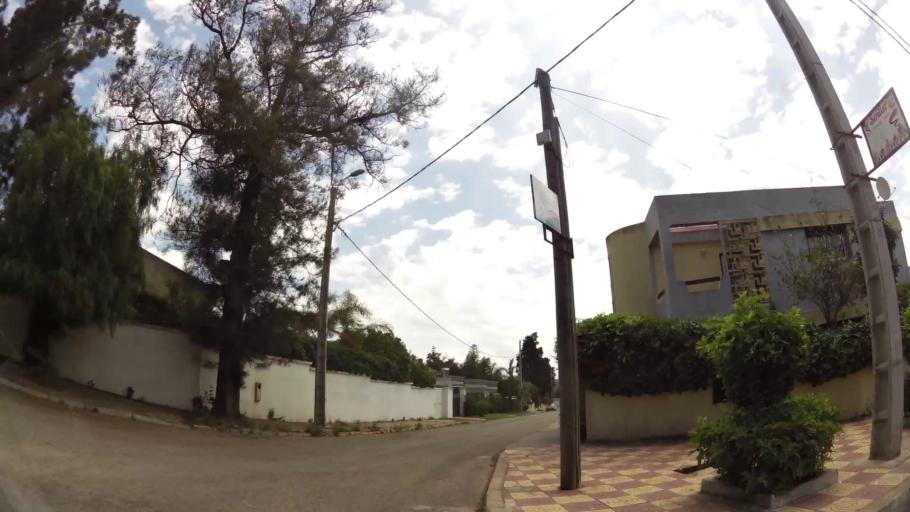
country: MA
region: Gharb-Chrarda-Beni Hssen
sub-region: Kenitra Province
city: Kenitra
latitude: 34.2636
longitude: -6.5982
